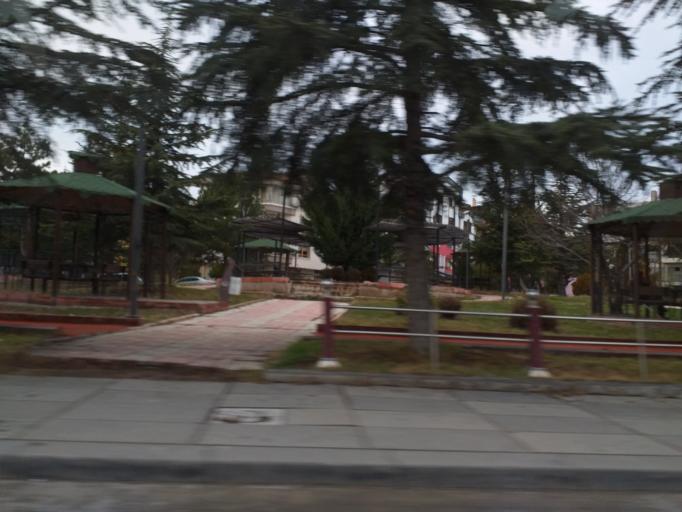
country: TR
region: Ankara
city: Ankara
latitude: 39.9779
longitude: 32.8196
